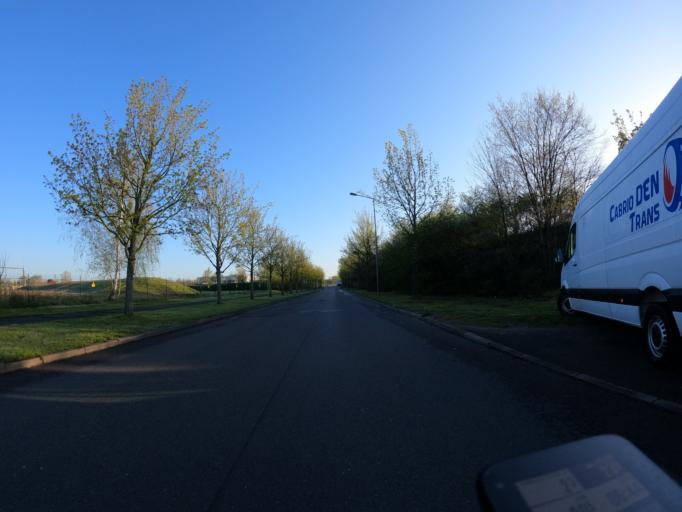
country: DE
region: Brandenburg
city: Altlandsberg
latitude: 52.5401
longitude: 13.7156
